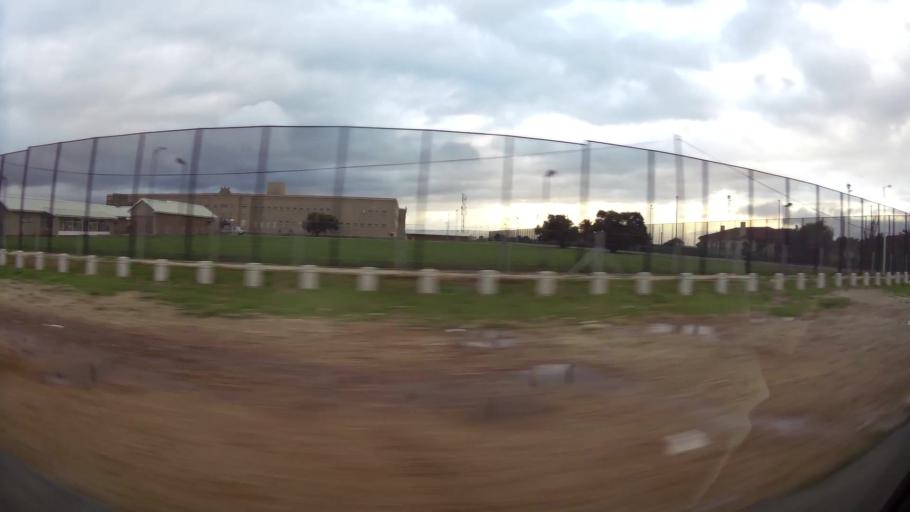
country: ZA
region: Eastern Cape
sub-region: Nelson Mandela Bay Metropolitan Municipality
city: Port Elizabeth
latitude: -33.9281
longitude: 25.6078
